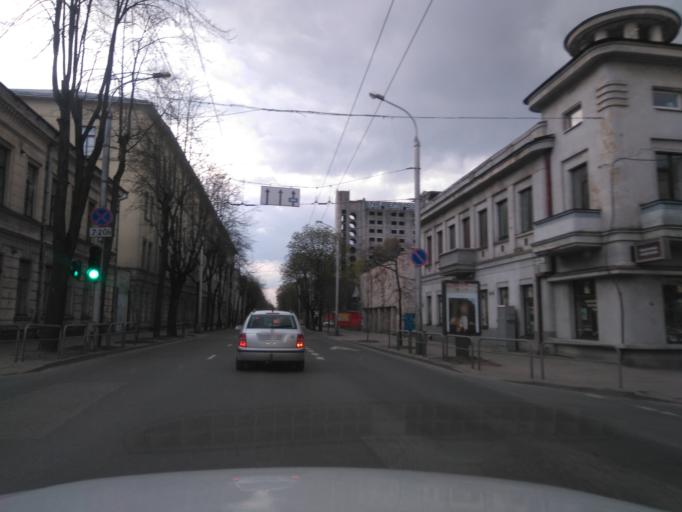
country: LT
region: Kauno apskritis
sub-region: Kaunas
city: Kaunas
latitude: 54.8954
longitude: 23.9214
